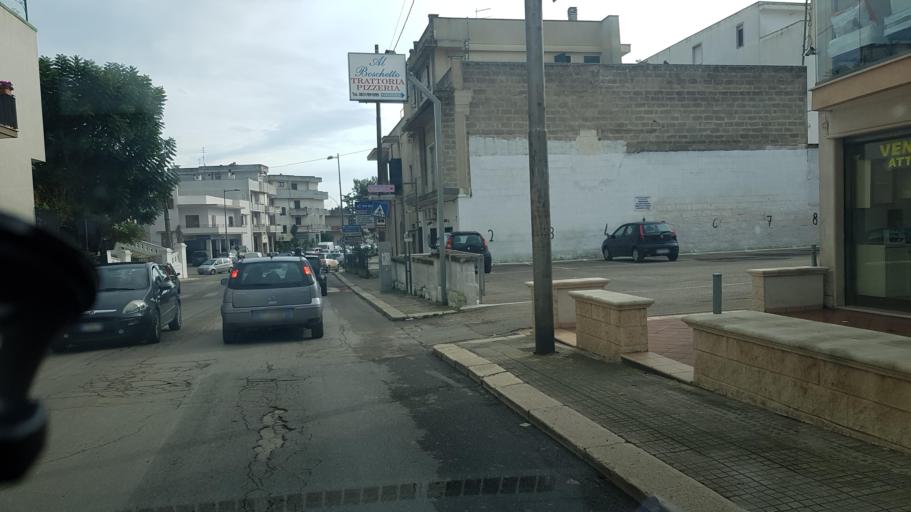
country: IT
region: Apulia
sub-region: Provincia di Brindisi
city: Carovigno
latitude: 40.7025
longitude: 17.6609
